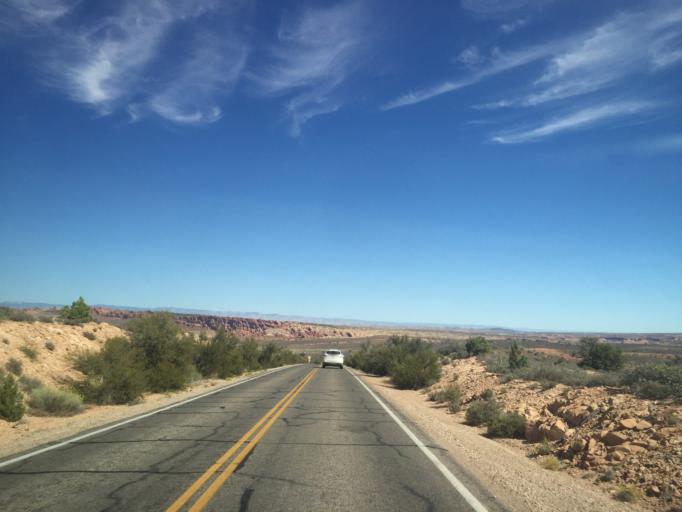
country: US
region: Utah
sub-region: Grand County
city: Moab
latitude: 38.7052
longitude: -109.5627
